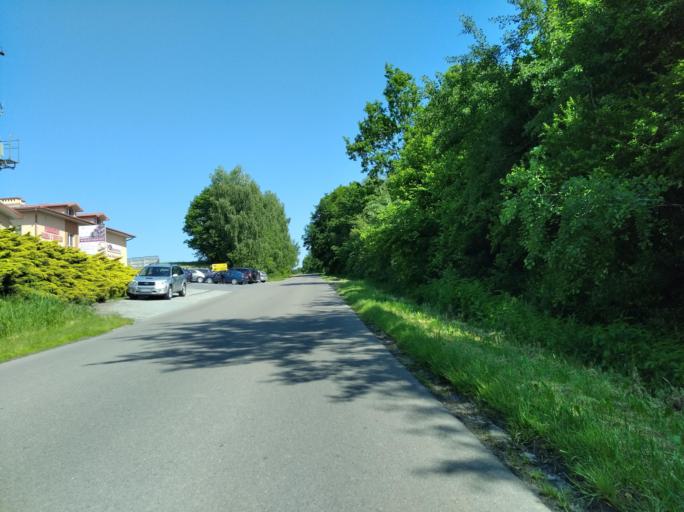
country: PL
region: Subcarpathian Voivodeship
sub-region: Powiat ropczycko-sedziszowski
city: Wielopole Skrzynskie
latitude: 49.9522
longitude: 21.6193
